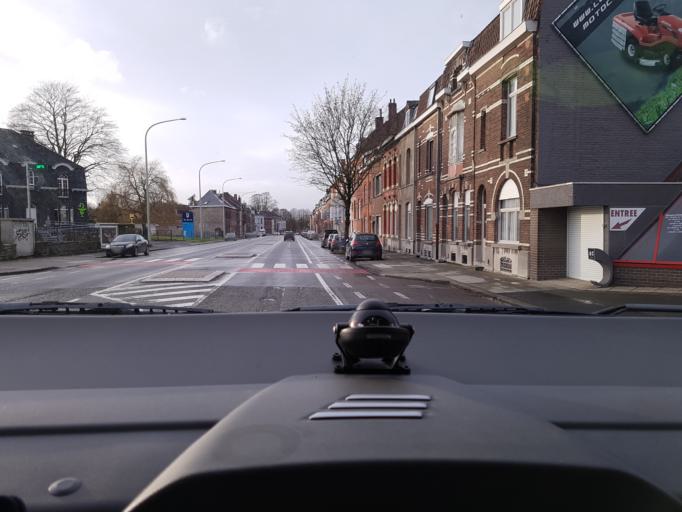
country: BE
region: Wallonia
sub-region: Province du Hainaut
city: Tournai
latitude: 50.6052
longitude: 3.4088
